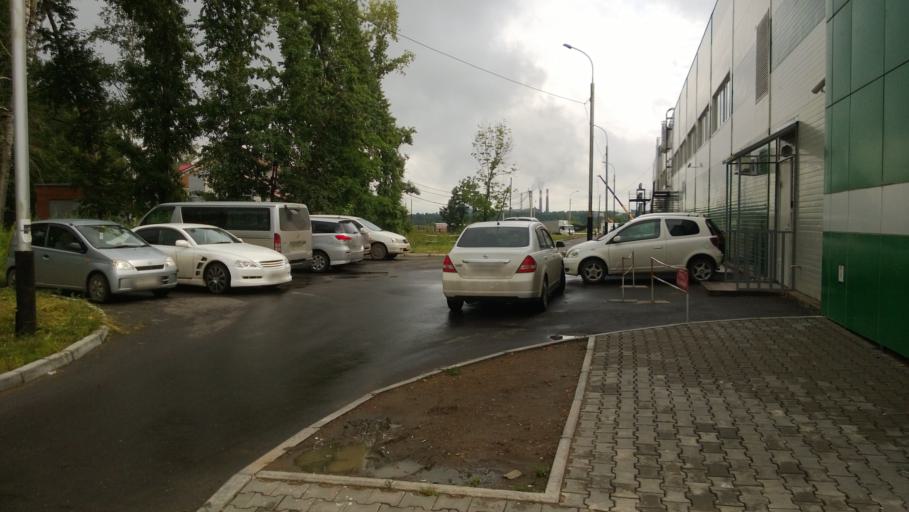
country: RU
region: Khabarovsk Krai
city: Khabarovsk Vtoroy
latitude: 48.3960
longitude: 135.1048
